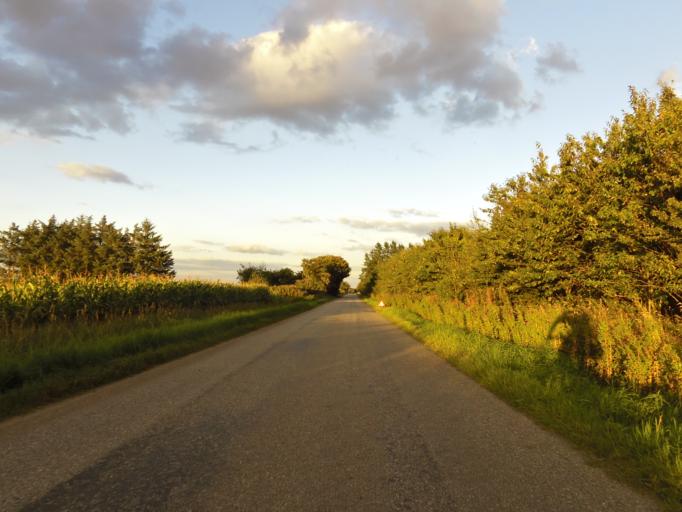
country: DK
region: South Denmark
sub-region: Tonder Kommune
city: Sherrebek
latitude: 55.2412
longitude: 8.8791
